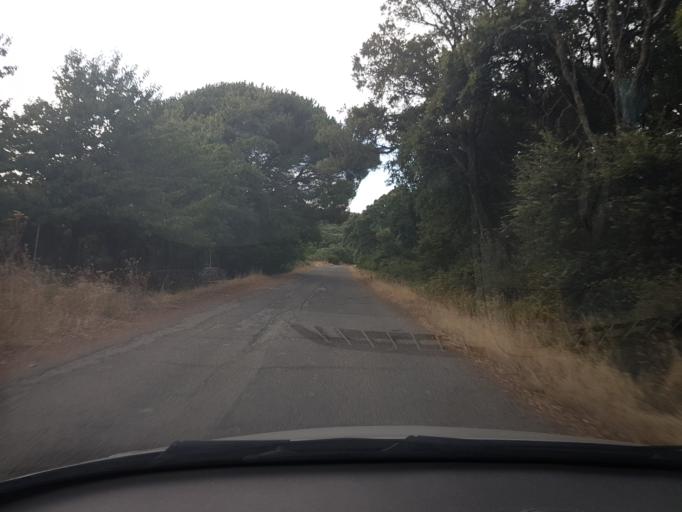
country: IT
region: Sardinia
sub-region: Provincia di Oristano
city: Seneghe
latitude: 40.1096
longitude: 8.6205
